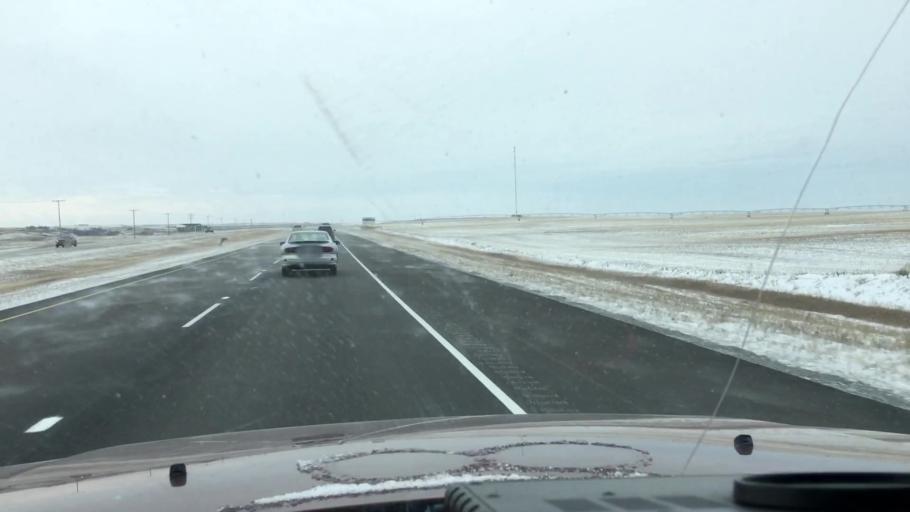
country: CA
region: Saskatchewan
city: Saskatoon
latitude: 51.7477
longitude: -106.4764
